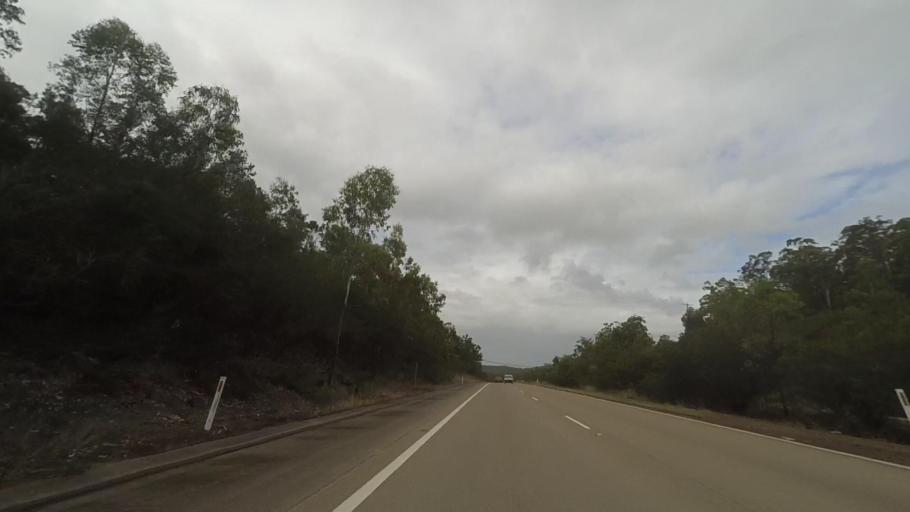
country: AU
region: New South Wales
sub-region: Port Stephens Shire
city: Medowie
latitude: -32.6310
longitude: 151.9398
